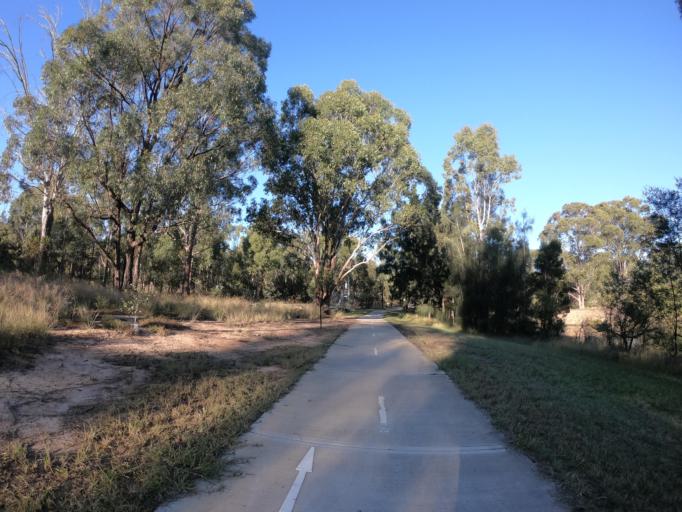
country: AU
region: New South Wales
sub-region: Hawkesbury
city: South Windsor
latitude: -33.6350
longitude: 150.8112
